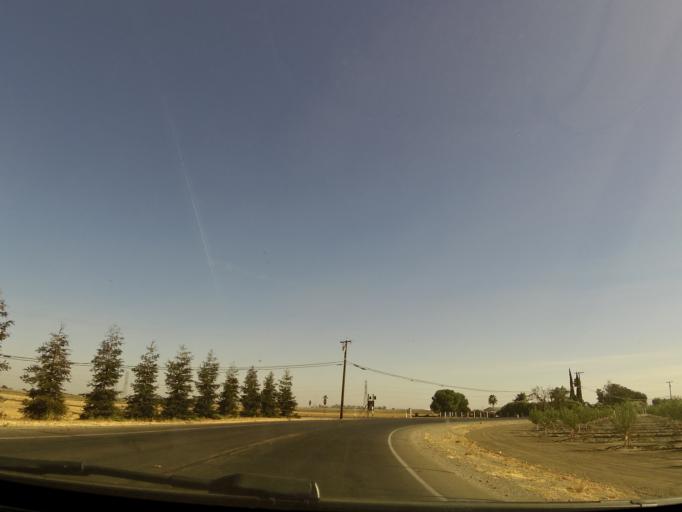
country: US
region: California
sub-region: San Joaquin County
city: Tracy
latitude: 37.7904
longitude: -121.4360
